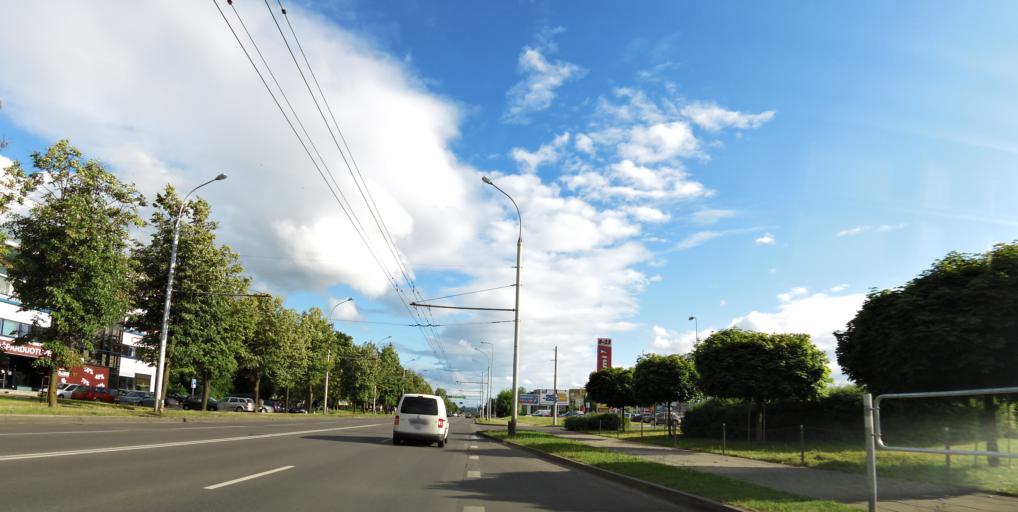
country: LT
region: Vilnius County
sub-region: Vilnius
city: Vilnius
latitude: 54.7137
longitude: 25.3050
